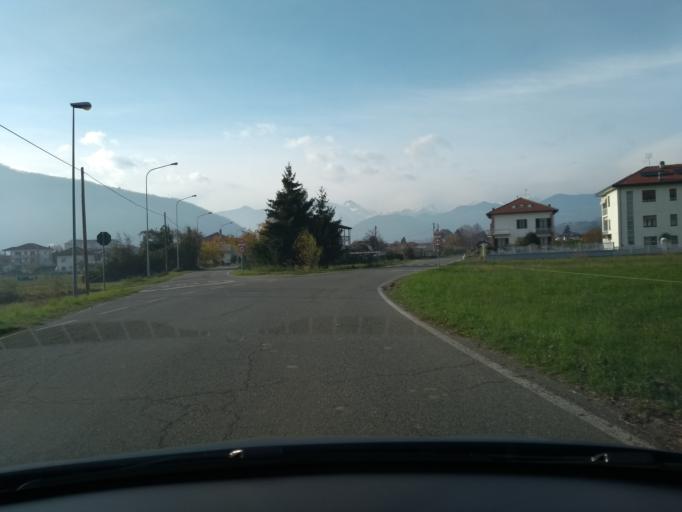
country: IT
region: Piedmont
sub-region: Provincia di Torino
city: Balangero
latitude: 45.2683
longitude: 7.5264
